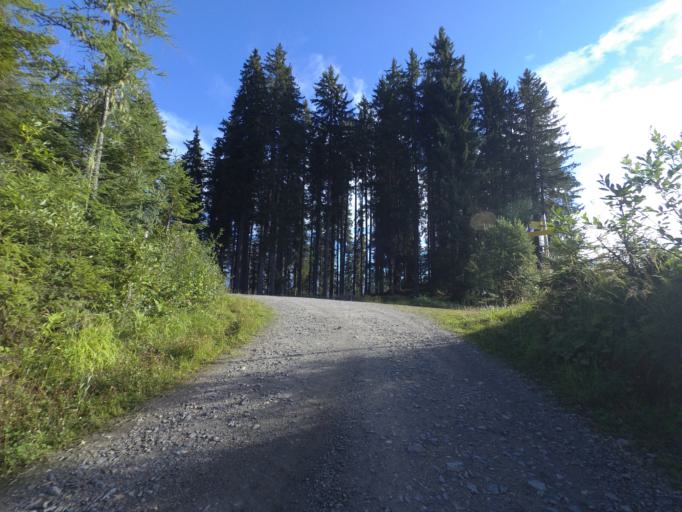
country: AT
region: Salzburg
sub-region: Politischer Bezirk Sankt Johann im Pongau
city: Muhlbach am Hochkonig
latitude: 47.3527
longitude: 13.1038
